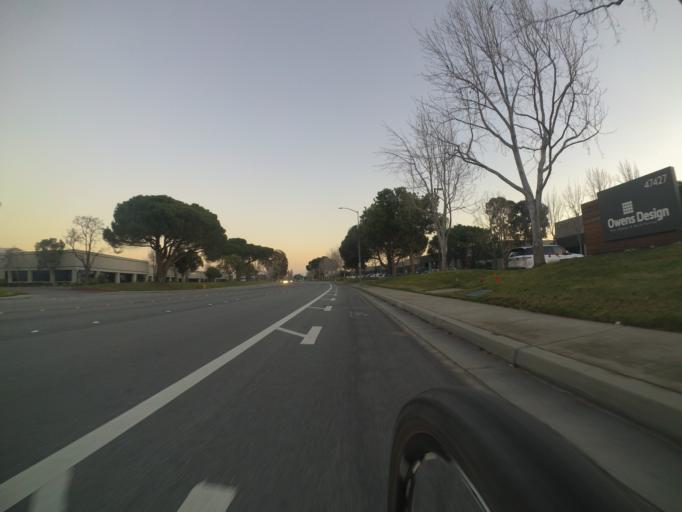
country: US
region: California
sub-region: Santa Clara County
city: Milpitas
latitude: 37.4760
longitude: -121.9445
